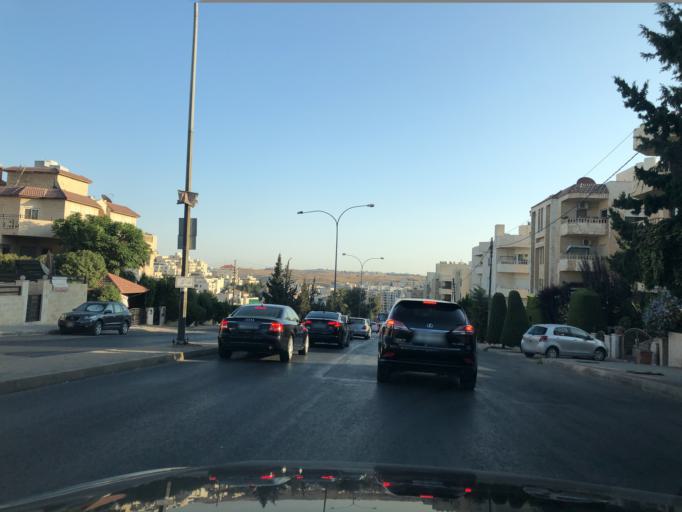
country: JO
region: Amman
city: Wadi as Sir
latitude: 31.9453
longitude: 35.8700
